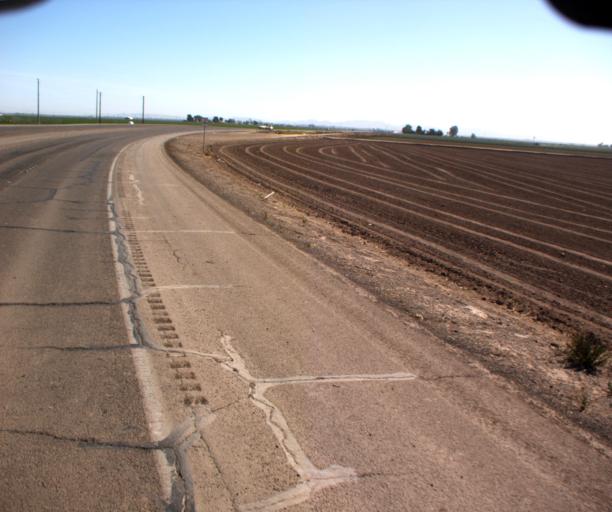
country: US
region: Arizona
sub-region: Yuma County
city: Somerton
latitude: 32.5668
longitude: -114.7825
